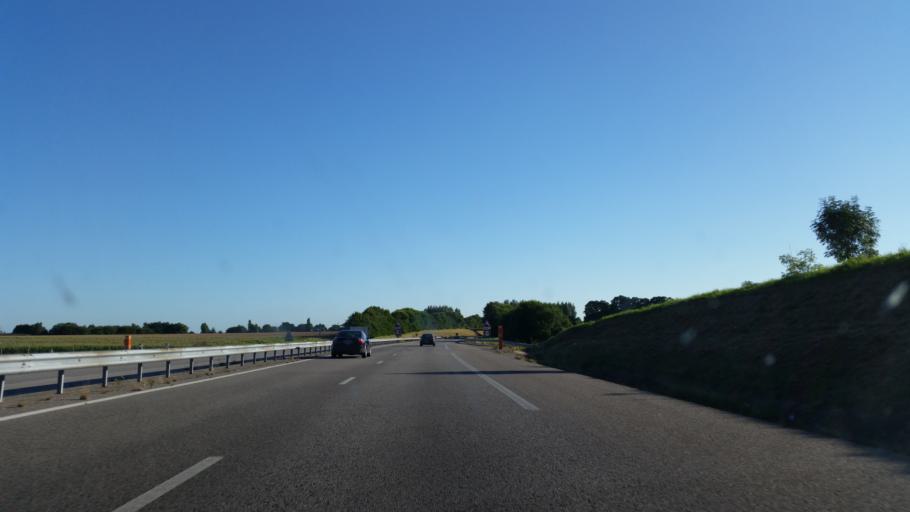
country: FR
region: Haute-Normandie
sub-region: Departement de la Seine-Maritime
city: Saint-Aubin-Routot
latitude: 49.5287
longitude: 0.3110
